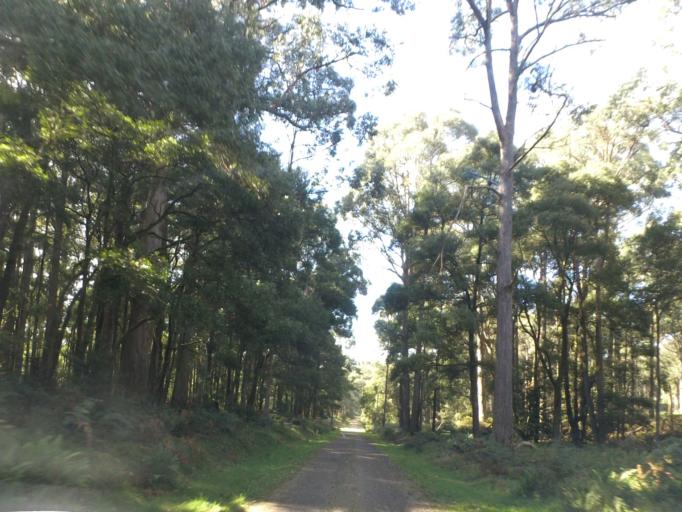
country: AU
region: Victoria
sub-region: Moorabool
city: Bacchus Marsh
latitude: -37.4318
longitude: 144.2156
